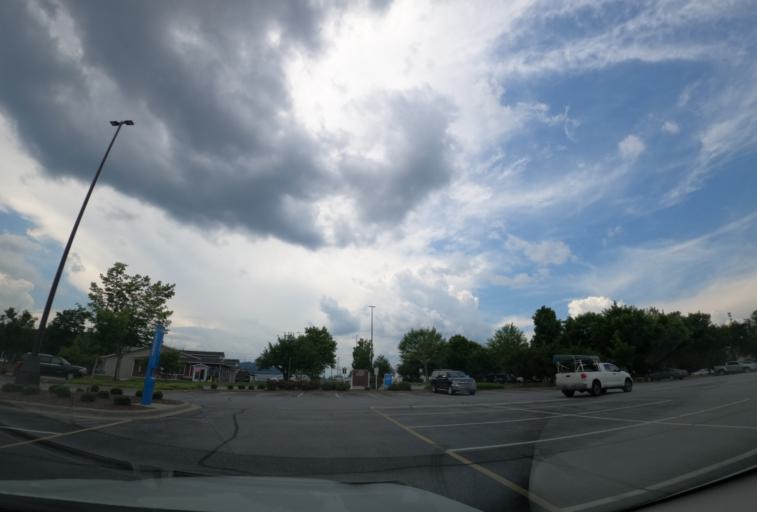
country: US
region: North Carolina
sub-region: Buncombe County
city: Bent Creek
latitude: 35.5276
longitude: -82.6052
